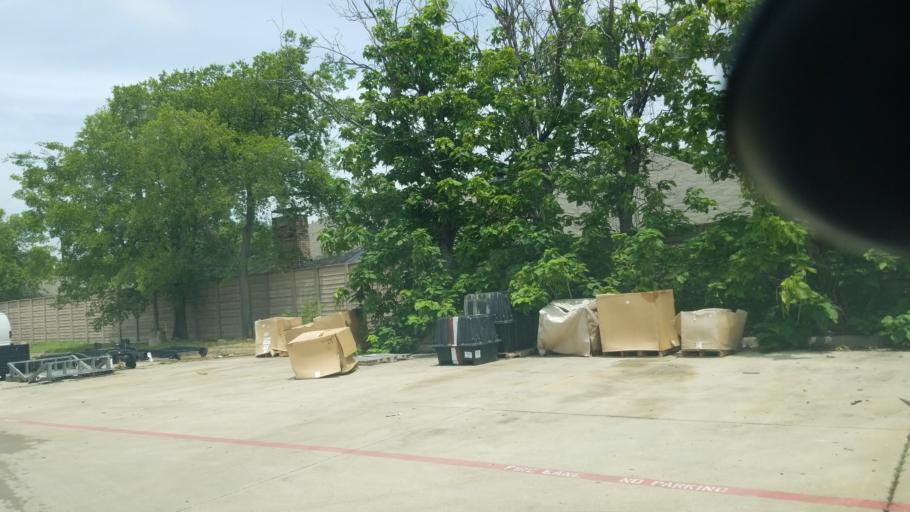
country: US
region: Texas
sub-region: Dallas County
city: Irving
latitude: 32.8407
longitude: -96.9551
